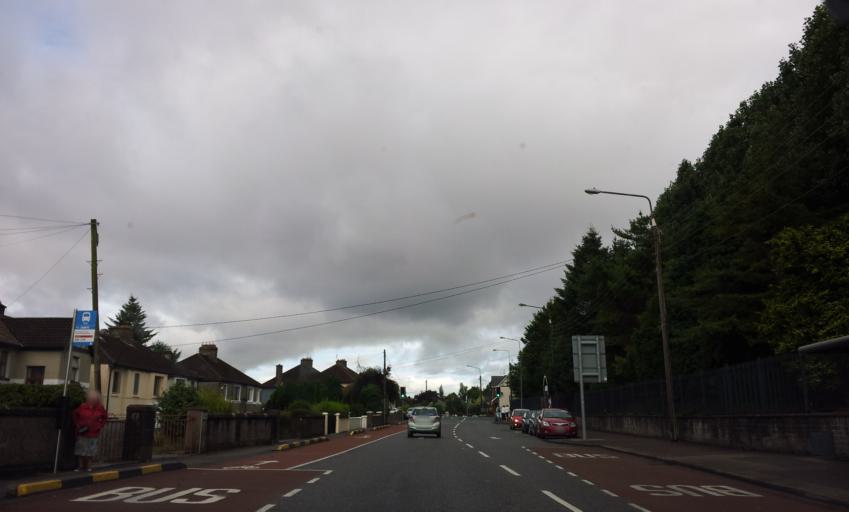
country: IE
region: Munster
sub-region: County Cork
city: Cork
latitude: 51.8774
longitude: -8.4421
